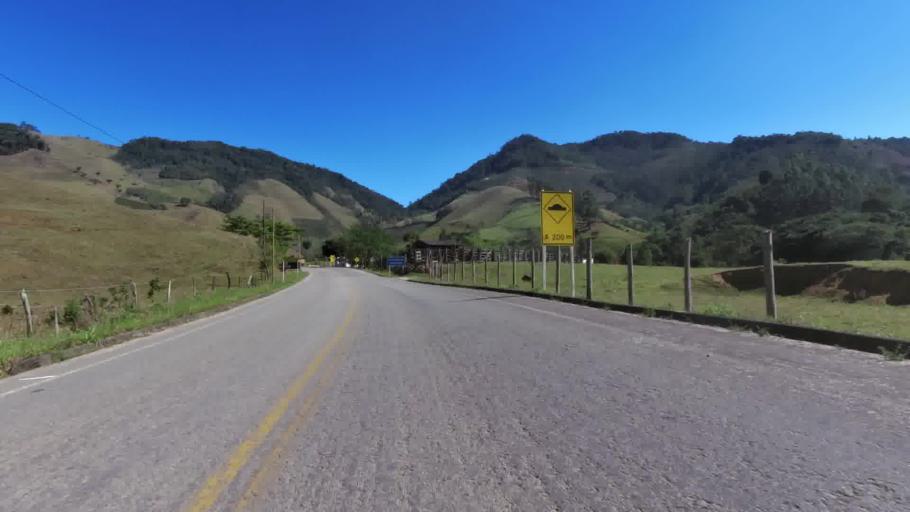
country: BR
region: Espirito Santo
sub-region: Vargem Alta
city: Vargem Alta
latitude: -20.7019
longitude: -40.9255
